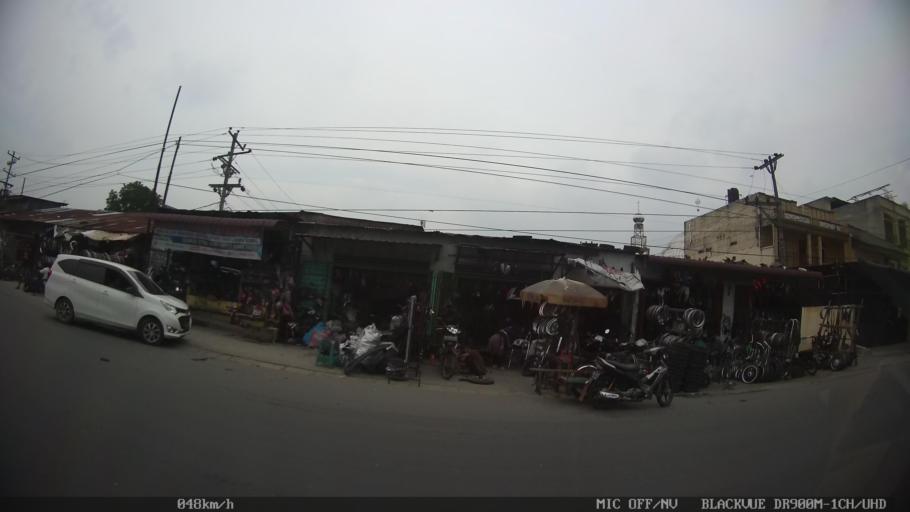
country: ID
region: North Sumatra
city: Deli Tua
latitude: 3.5382
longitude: 98.6875
